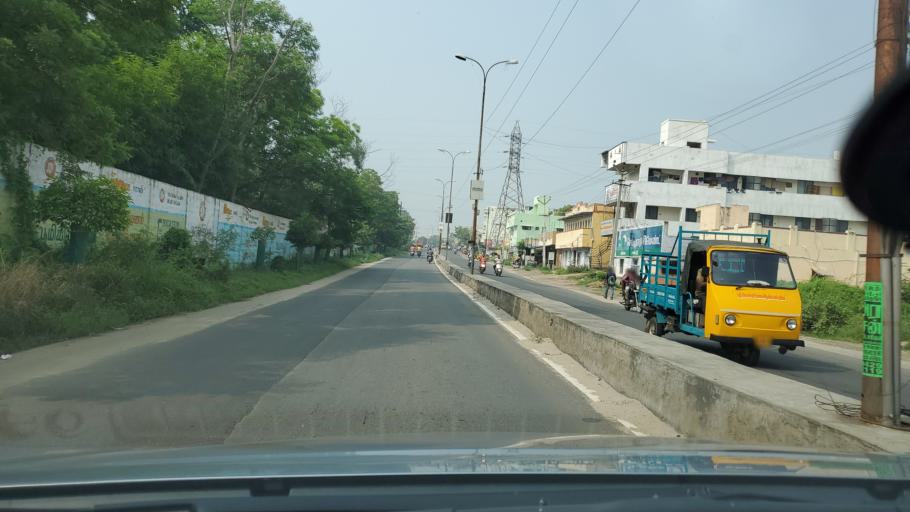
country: IN
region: Tamil Nadu
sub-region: Erode
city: Erode
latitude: 11.3267
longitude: 77.7198
